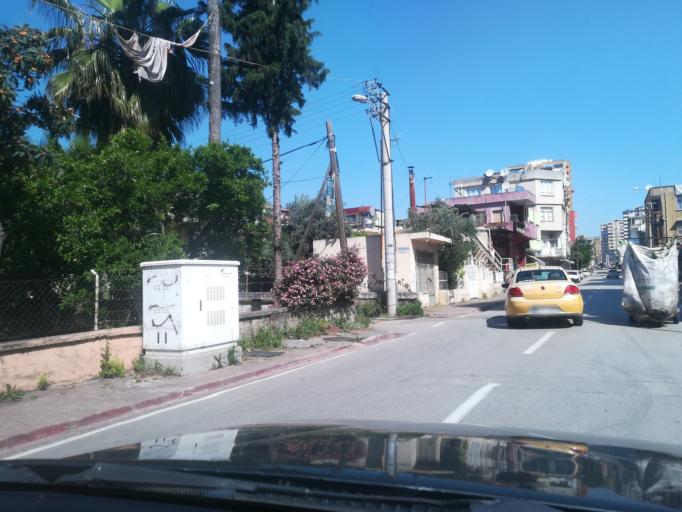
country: TR
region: Adana
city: Adana
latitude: 37.0077
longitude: 35.3213
